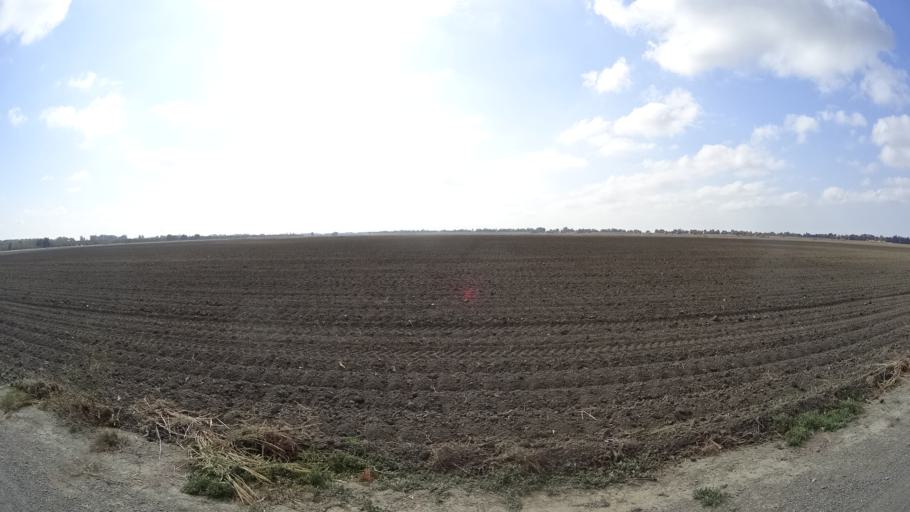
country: US
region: California
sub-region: Yolo County
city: Woodland
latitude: 38.7958
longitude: -121.7067
